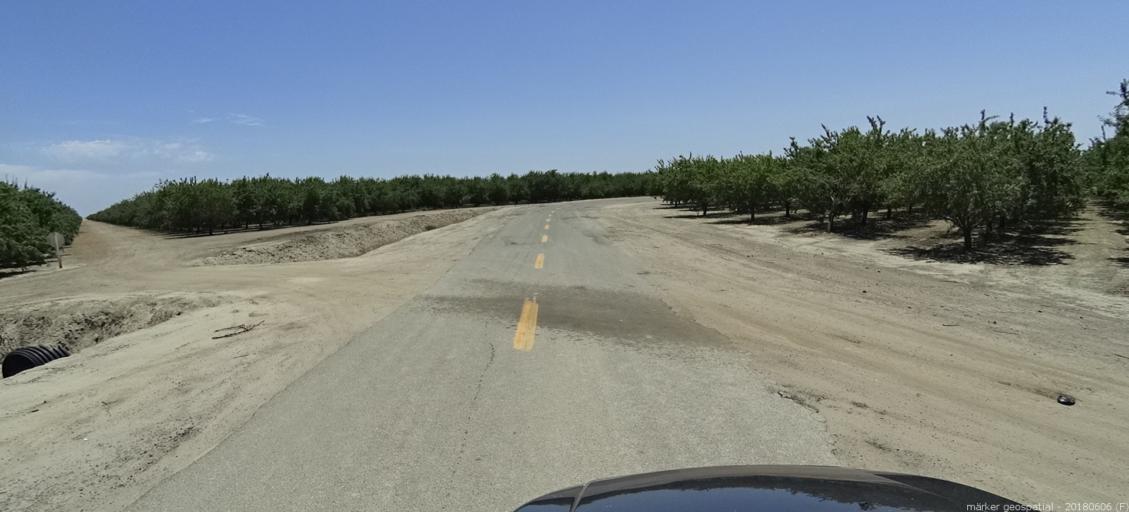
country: US
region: California
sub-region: Fresno County
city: Mendota
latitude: 36.8151
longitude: -120.3651
